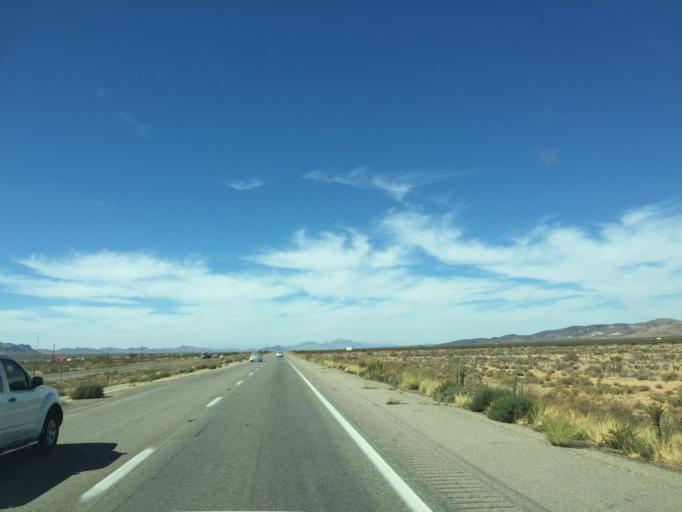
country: US
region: Arizona
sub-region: Mohave County
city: Dolan Springs
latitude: 35.5614
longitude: -114.3742
